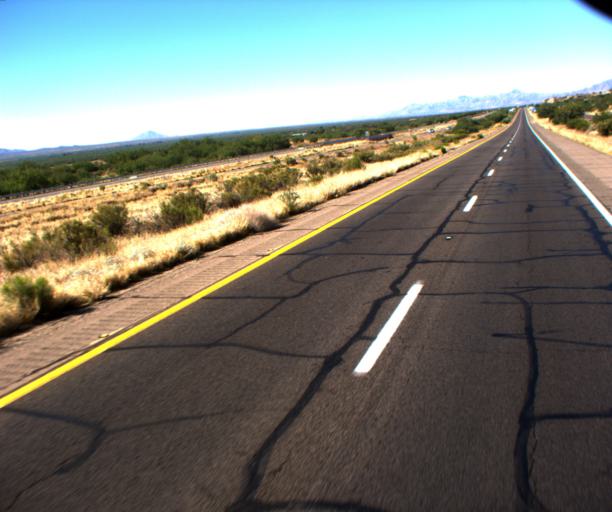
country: US
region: Arizona
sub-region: Pima County
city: Green Valley
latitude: 31.8022
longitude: -111.0153
